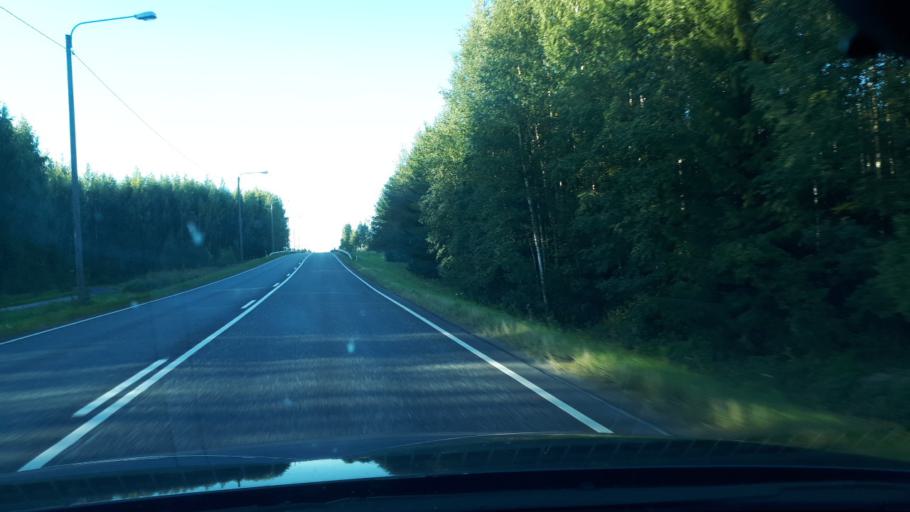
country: FI
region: Northern Savo
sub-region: Ylae-Savo
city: Lapinlahti
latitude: 63.4295
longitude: 27.3283
